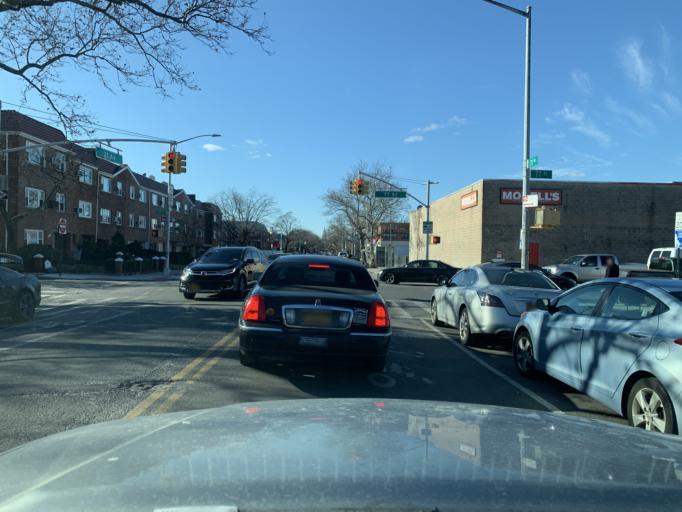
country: US
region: New York
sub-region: Queens County
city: Long Island City
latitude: 40.7588
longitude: -73.8904
